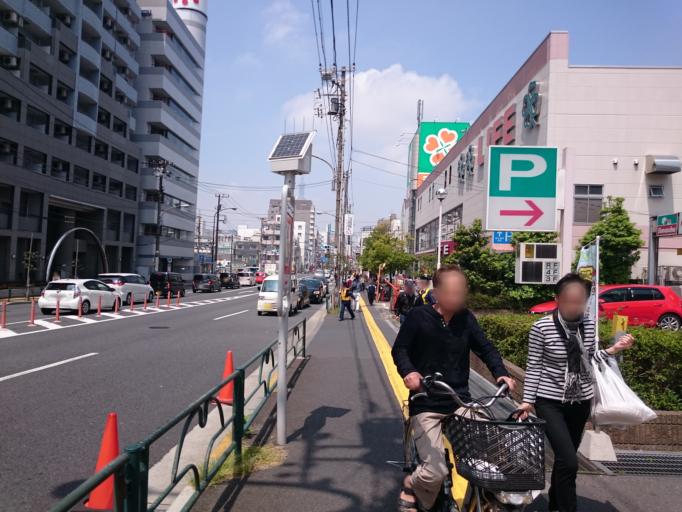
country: JP
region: Tokyo
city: Urayasu
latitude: 35.6854
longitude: 139.8161
